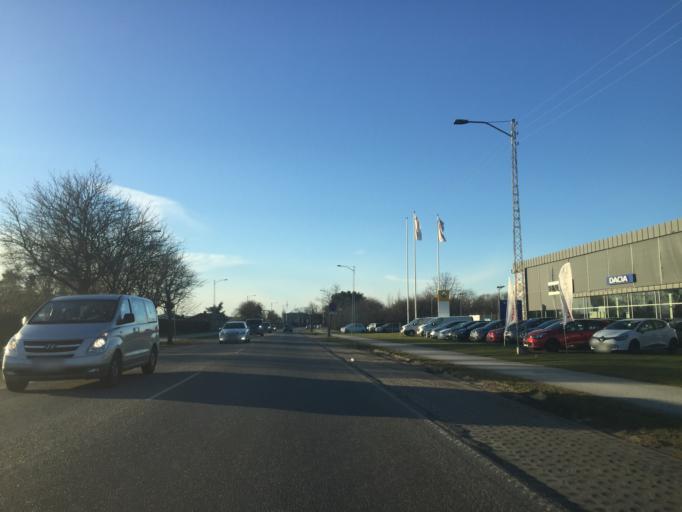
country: DK
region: Capital Region
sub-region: Tarnby Kommune
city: Tarnby
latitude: 55.6163
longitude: 12.6085
